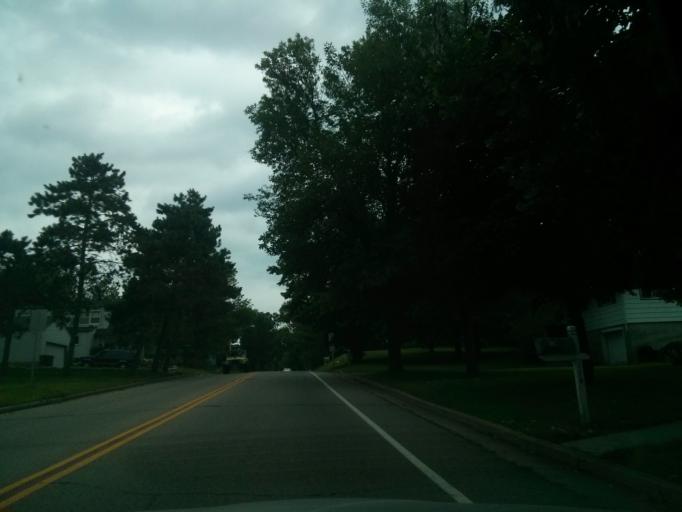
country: US
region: Wisconsin
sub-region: Saint Croix County
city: Hudson
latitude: 44.9709
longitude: -92.7437
